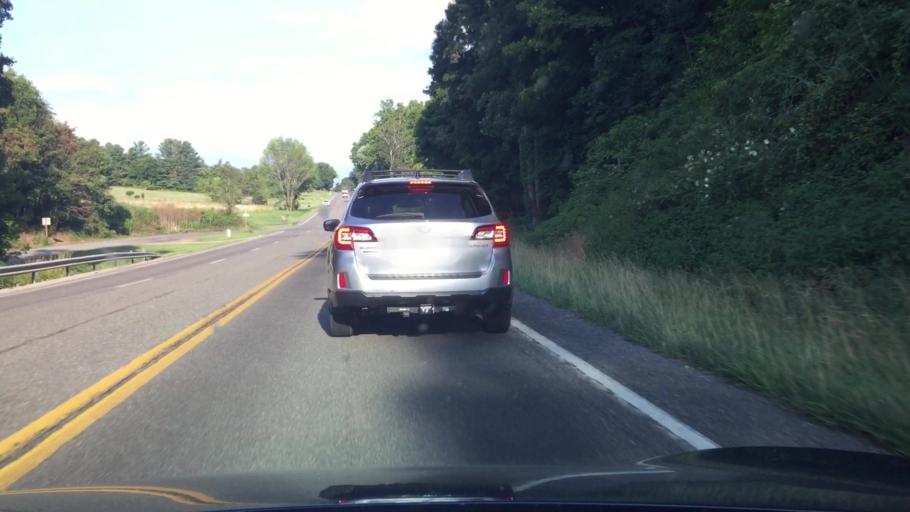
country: US
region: Virginia
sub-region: Montgomery County
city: Christiansburg
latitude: 37.1319
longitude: -80.4565
